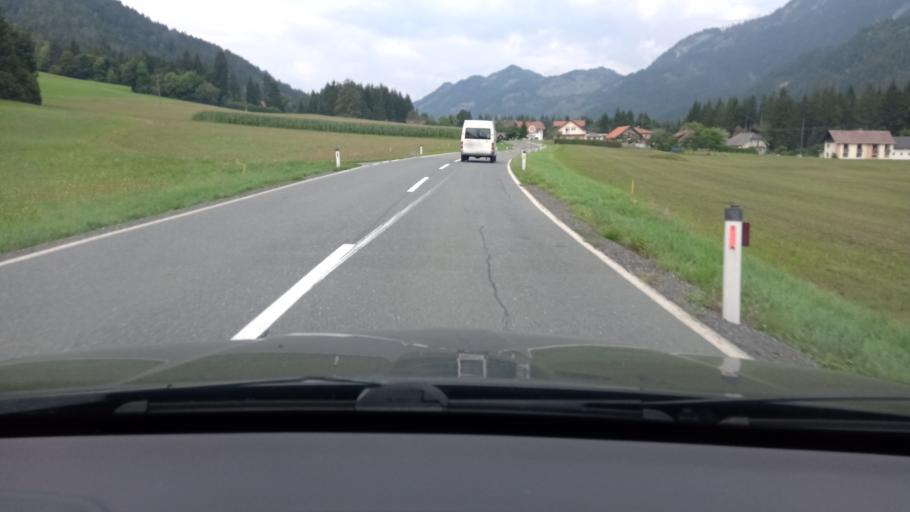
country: AT
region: Carinthia
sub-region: Politischer Bezirk Hermagor
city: Hermagor
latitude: 46.6433
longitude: 13.3386
